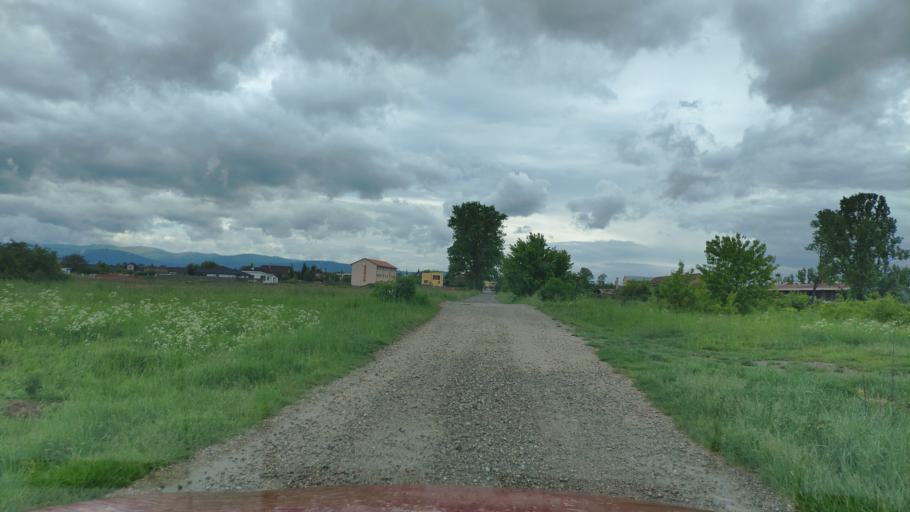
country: SK
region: Kosicky
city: Moldava nad Bodvou
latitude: 48.5675
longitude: 21.1214
